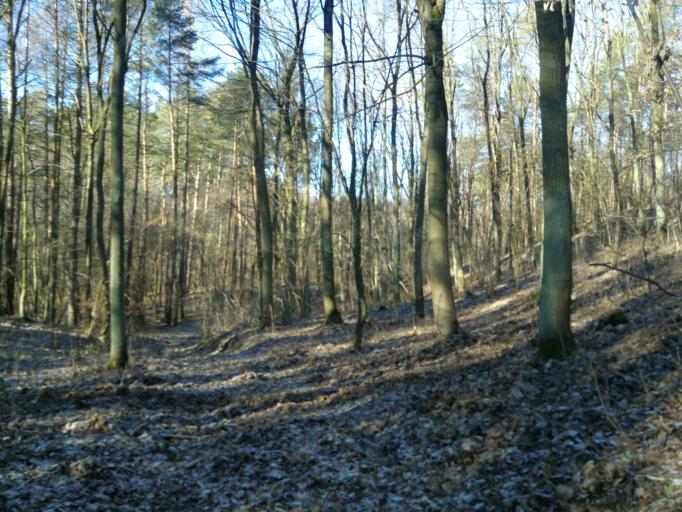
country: PL
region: Kujawsko-Pomorskie
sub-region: Powiat brodnicki
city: Gorzno
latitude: 53.2201
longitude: 19.6652
